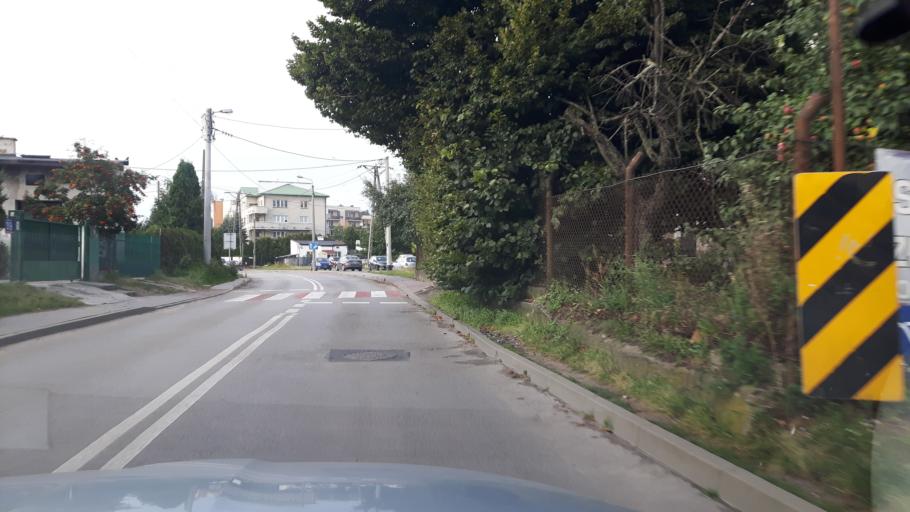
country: PL
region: Masovian Voivodeship
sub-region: Powiat wolominski
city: Marki
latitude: 52.3284
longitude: 21.1017
